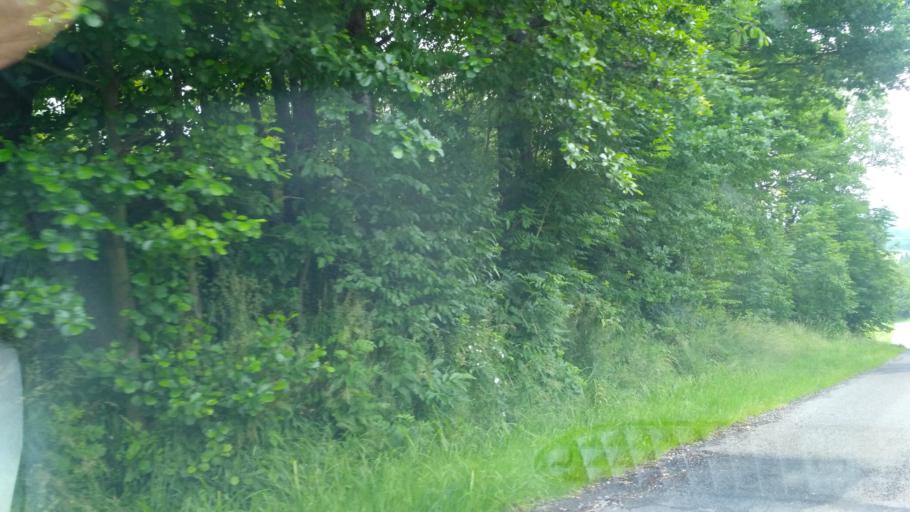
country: PL
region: Subcarpathian Voivodeship
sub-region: Powiat przemyski
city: Nienadowa
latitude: 49.8611
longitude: 22.4096
